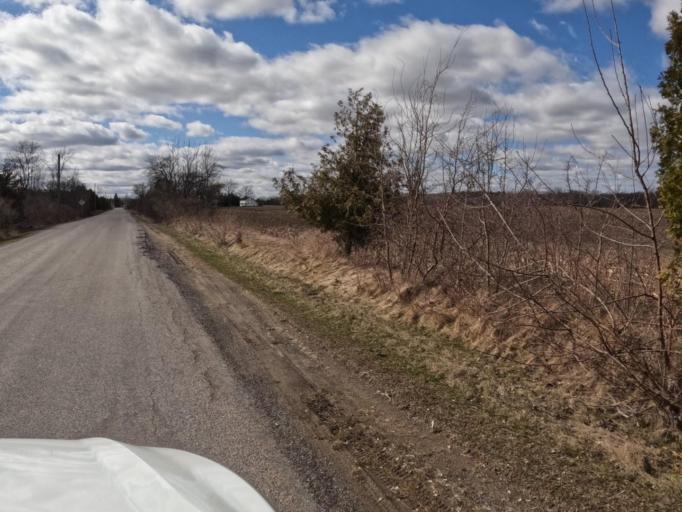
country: CA
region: Ontario
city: Norfolk County
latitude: 42.7552
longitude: -80.2682
